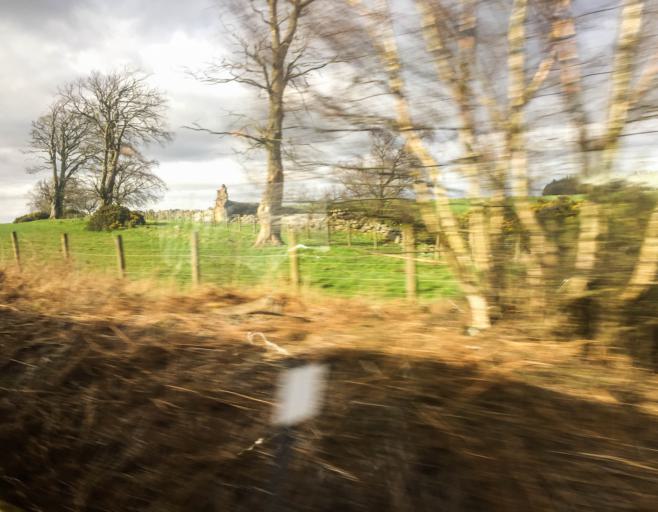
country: GB
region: Scotland
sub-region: South Lanarkshire
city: Carluke
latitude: 55.7029
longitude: -3.8126
